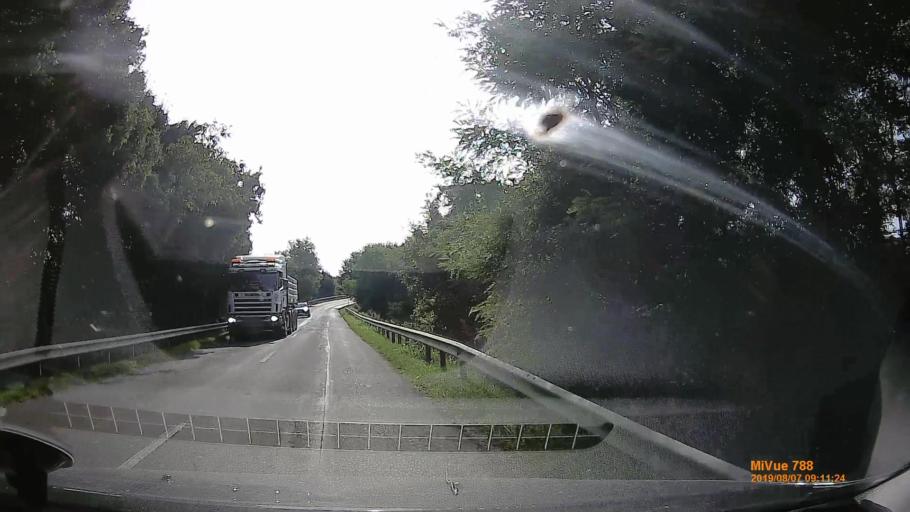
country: HU
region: Zala
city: Sarmellek
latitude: 46.7244
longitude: 17.0929
